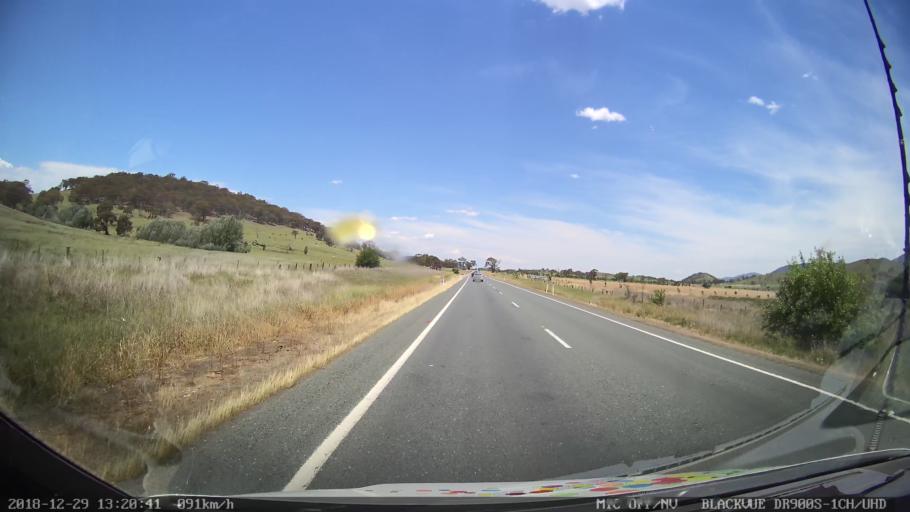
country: AU
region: Australian Capital Territory
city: Macarthur
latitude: -35.7821
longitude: 149.1619
